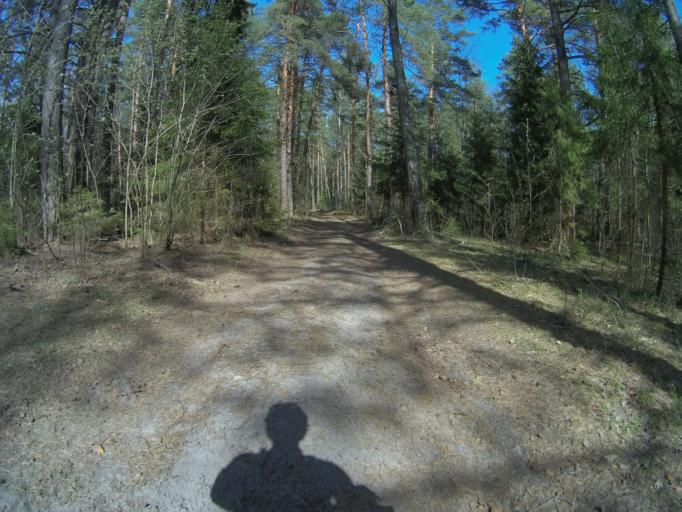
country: RU
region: Vladimir
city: Bogolyubovo
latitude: 56.1246
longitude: 40.5383
